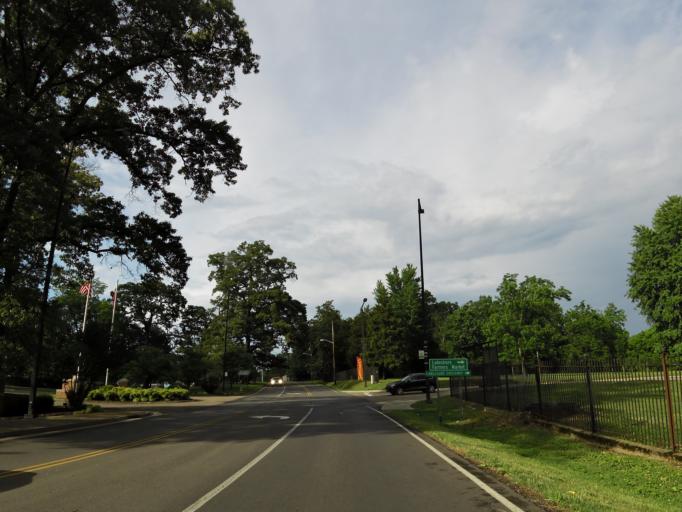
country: US
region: Tennessee
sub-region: Knox County
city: Knoxville
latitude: 35.9248
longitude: -83.9936
